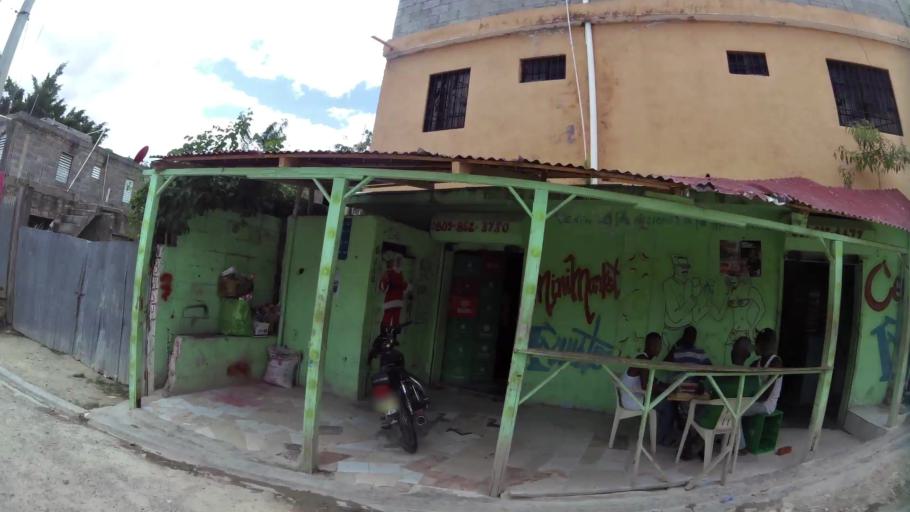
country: DO
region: Nacional
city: Ensanche Luperon
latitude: 18.5163
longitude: -69.9037
